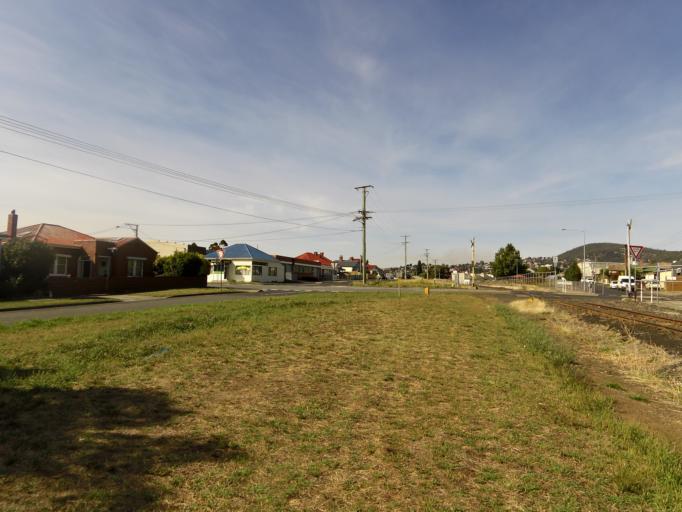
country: AU
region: Tasmania
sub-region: Glenorchy
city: Moonah
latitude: -42.8473
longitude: 147.2984
